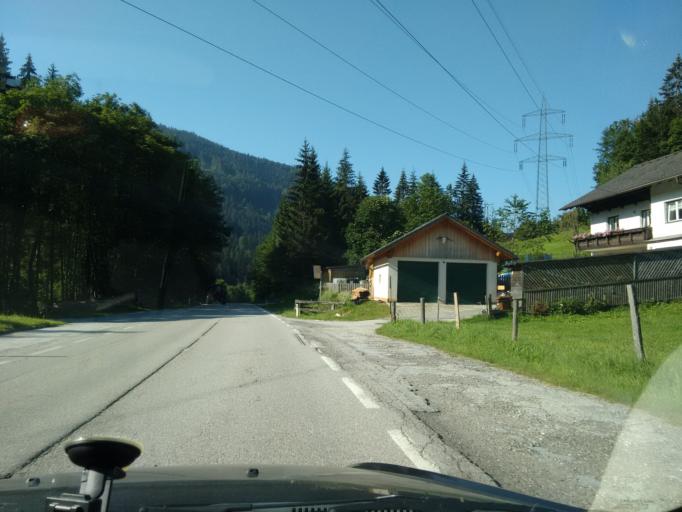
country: AT
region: Styria
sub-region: Politischer Bezirk Liezen
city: Liezen
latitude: 47.5873
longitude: 14.2751
